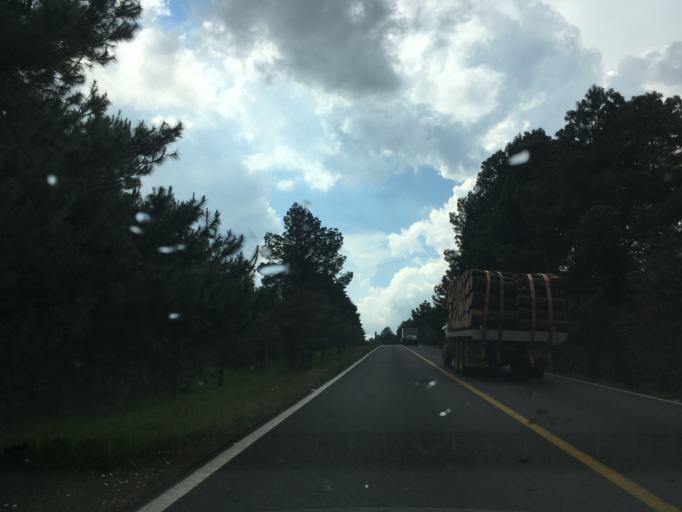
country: MX
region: Michoacan
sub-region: Patzcuaro
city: Santa Maria Huiramangaro (San Juan Tumbio)
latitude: 19.4901
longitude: -101.7942
